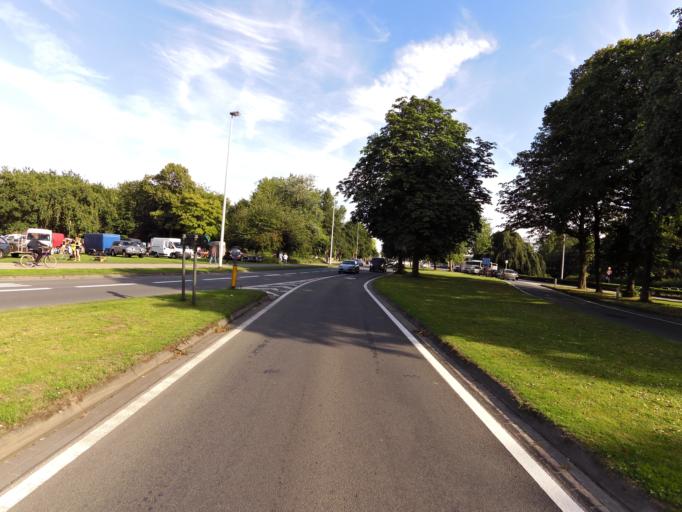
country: BE
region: Flanders
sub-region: Provincie West-Vlaanderen
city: Brugge
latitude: 51.1998
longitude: 3.2186
